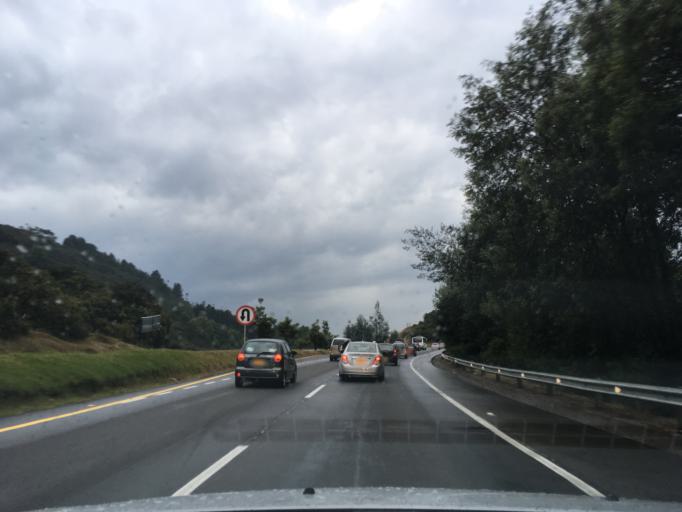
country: CO
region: Cundinamarca
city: Suesca
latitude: 5.0832
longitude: -73.7449
